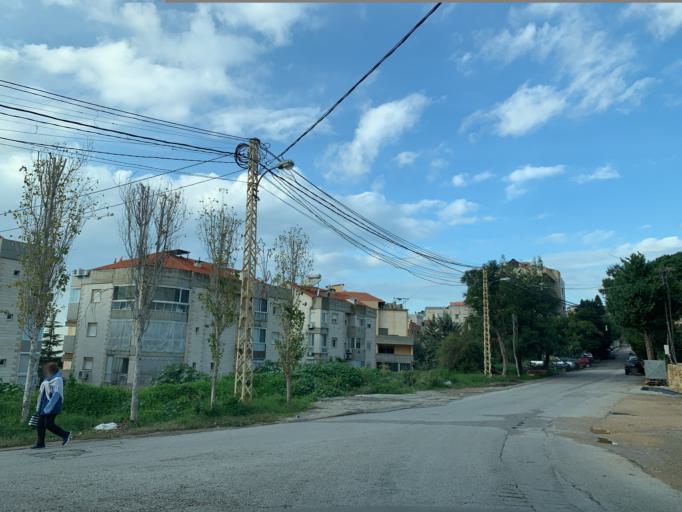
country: LB
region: Mont-Liban
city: Baabda
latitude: 33.8520
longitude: 35.5772
